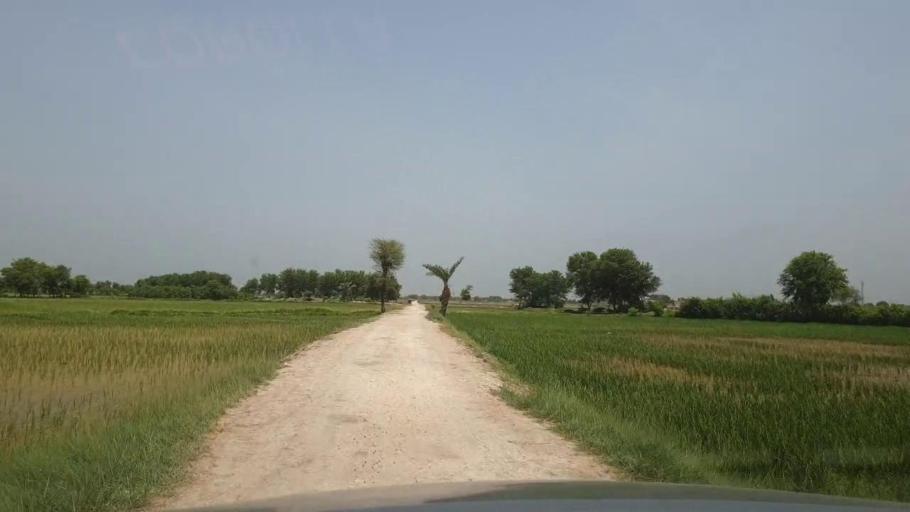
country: PK
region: Sindh
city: Madeji
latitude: 27.7580
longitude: 68.3741
